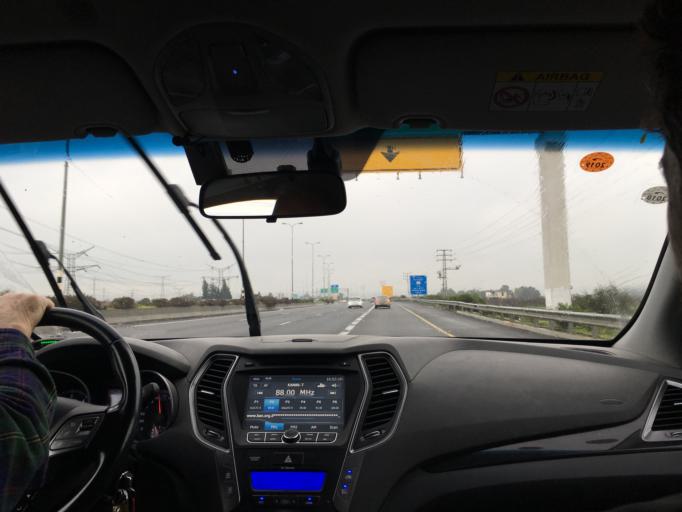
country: IL
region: Central District
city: Rosh Ha'Ayin
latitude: 32.1177
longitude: 34.9200
